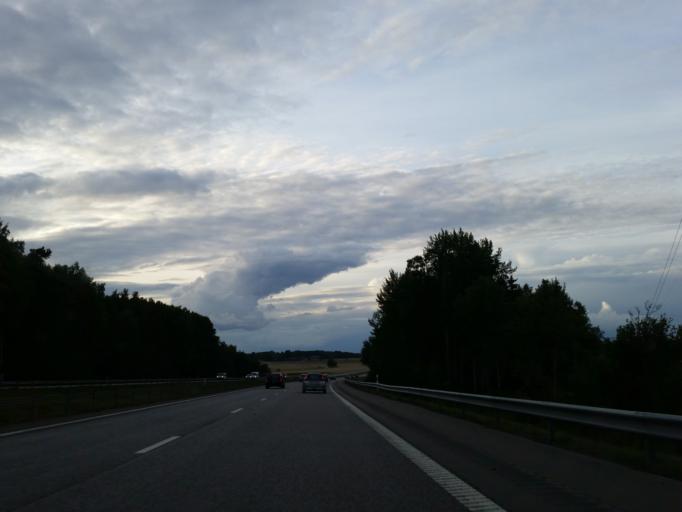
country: SE
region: Uppsala
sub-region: Uppsala Kommun
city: Alsike
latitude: 59.8030
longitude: 17.7655
